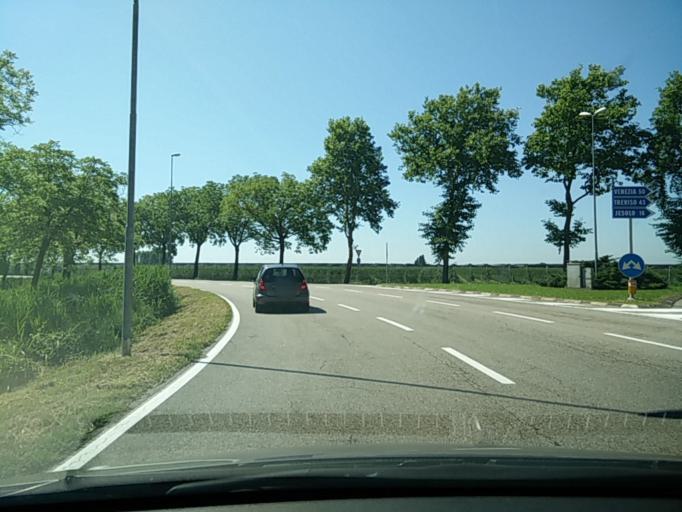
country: IT
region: Veneto
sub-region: Provincia di Venezia
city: San Giorgio di Livenza
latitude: 45.6349
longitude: 12.7462
